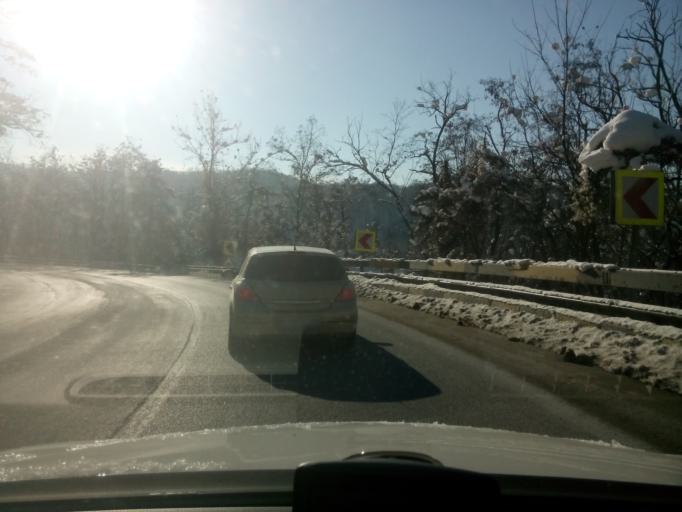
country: RO
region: Valcea
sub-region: Comuna Milcoiu
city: Milcoiu
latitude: 45.0563
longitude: 24.4531
